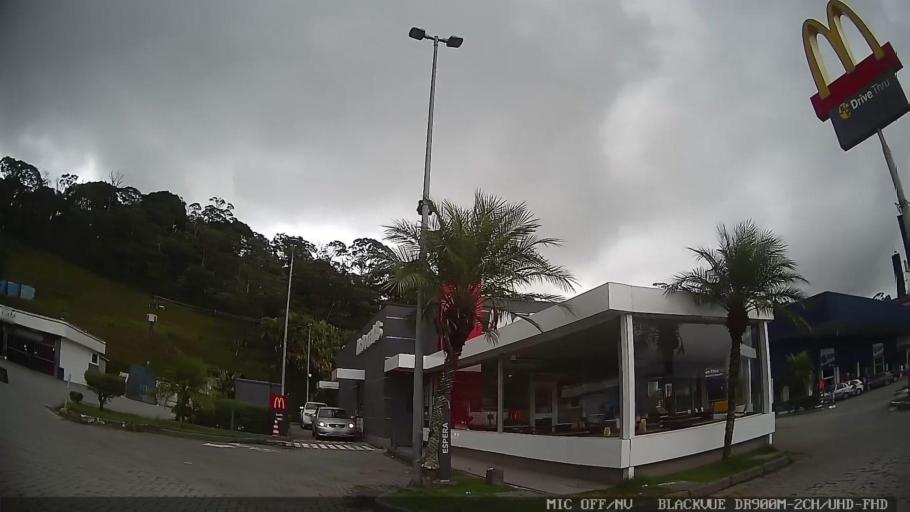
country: BR
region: Sao Paulo
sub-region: Sao Bernardo Do Campo
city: Sao Bernardo do Campo
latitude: -23.8401
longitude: -46.5757
